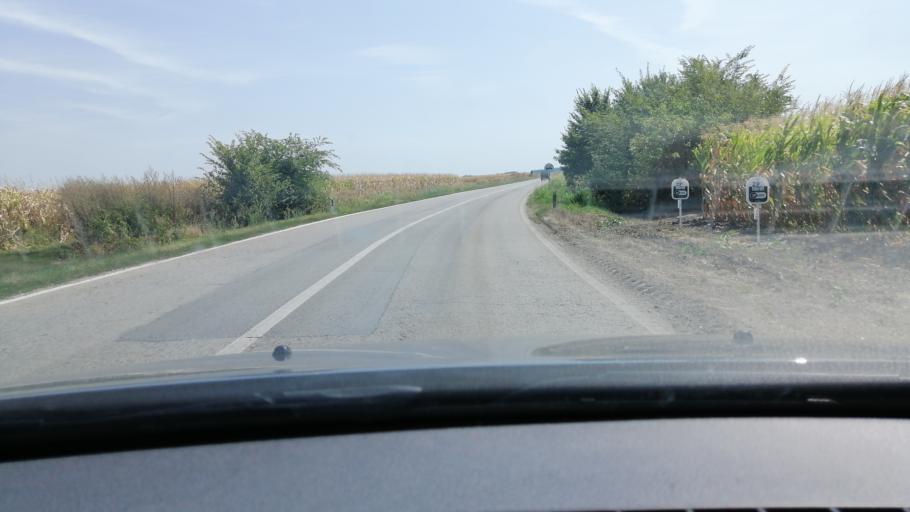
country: RS
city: Sutjeska
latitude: 45.3813
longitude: 20.7269
